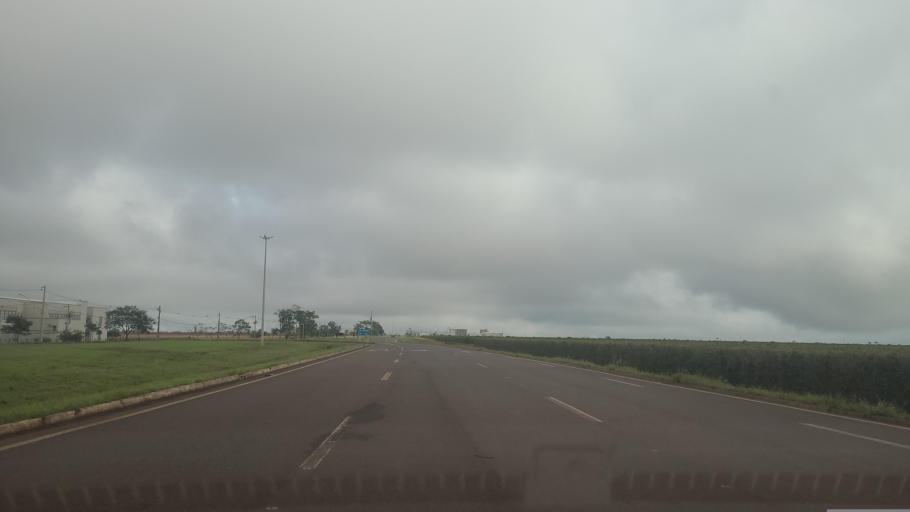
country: BR
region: Minas Gerais
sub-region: Sao Gotardo
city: Sao Gotardo
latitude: -19.2168
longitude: -46.2214
